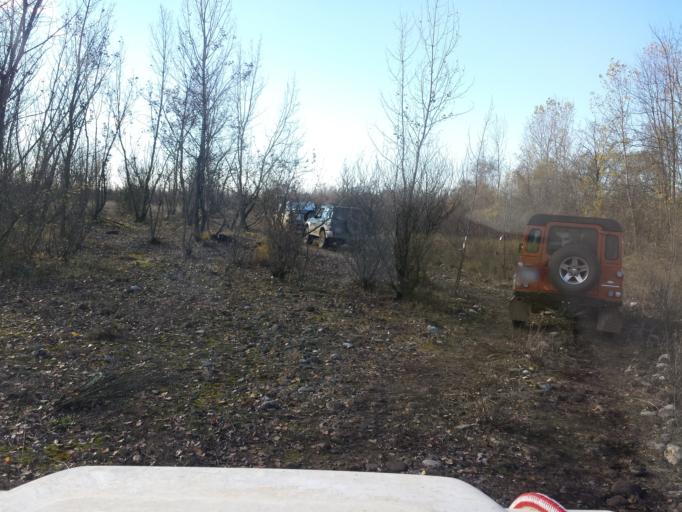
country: IT
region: Friuli Venezia Giulia
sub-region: Provincia di Udine
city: San Giovanni al Natisone
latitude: 45.9758
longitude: 13.3878
